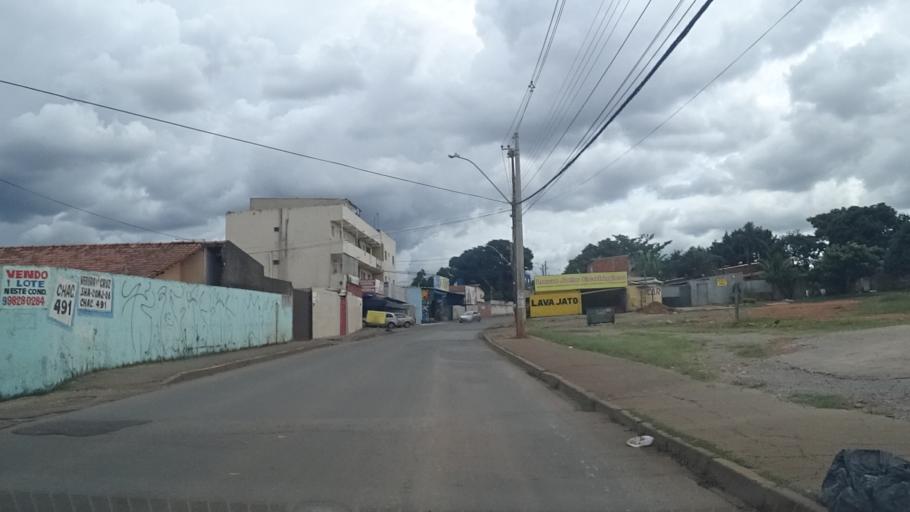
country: BR
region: Federal District
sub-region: Brasilia
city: Brasilia
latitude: -15.8508
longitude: -48.0288
